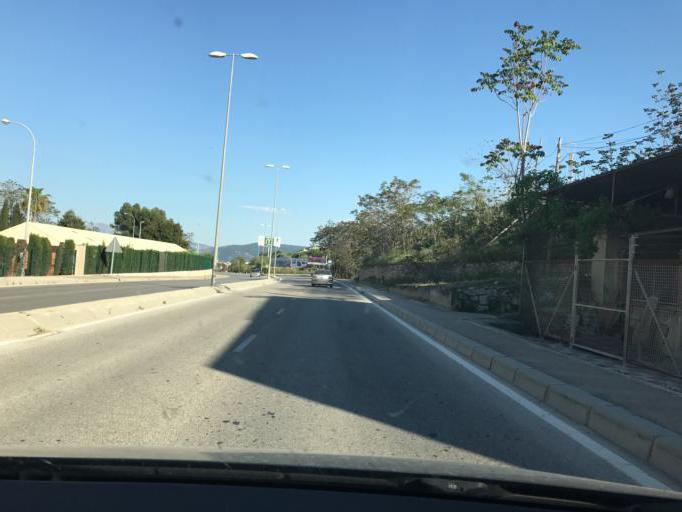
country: ES
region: Andalusia
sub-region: Provincia de Jaen
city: Jaen
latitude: 37.7832
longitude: -3.8256
